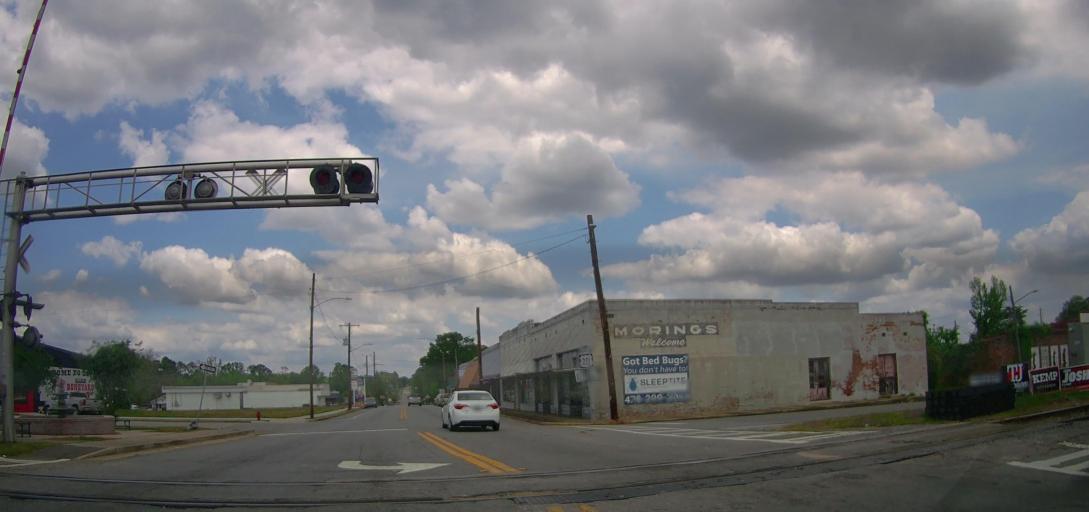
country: US
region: Georgia
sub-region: Treutlen County
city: Soperton
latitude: 32.3777
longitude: -82.5920
